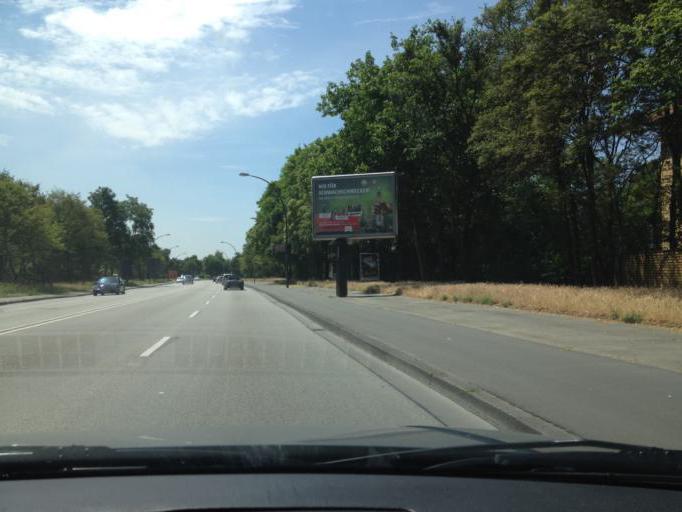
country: DE
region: Rheinland-Pfalz
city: Ludwigshafen am Rhein
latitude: 49.4609
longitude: 8.4358
